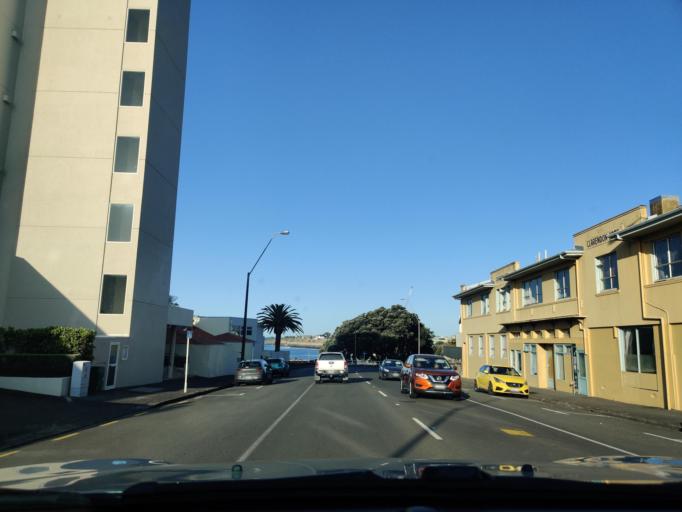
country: NZ
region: Taranaki
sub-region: New Plymouth District
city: New Plymouth
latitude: -39.0568
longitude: 174.0680
